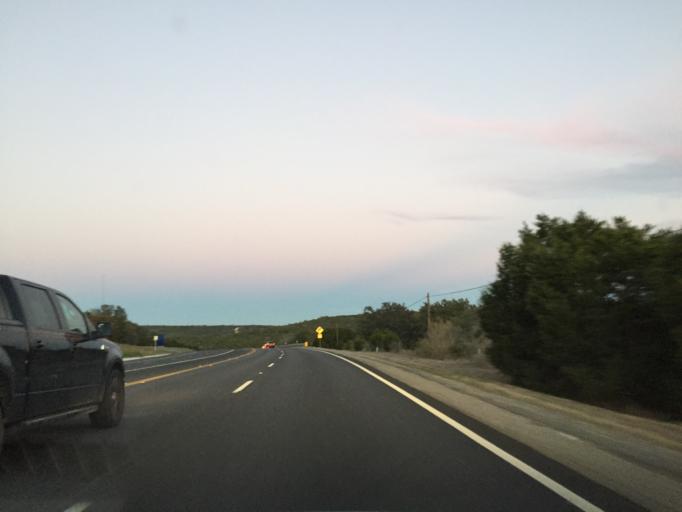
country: US
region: Texas
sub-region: Travis County
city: Jonestown
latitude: 30.5189
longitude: -97.9016
